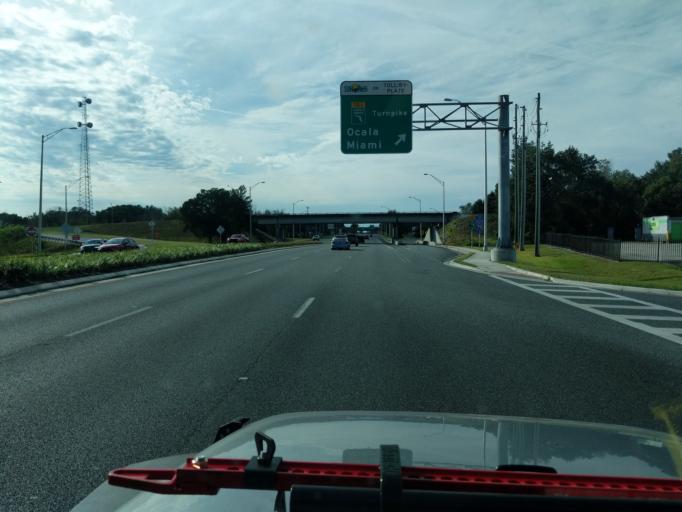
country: US
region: Florida
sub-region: Orange County
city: Ocoee
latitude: 28.5517
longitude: -81.5503
